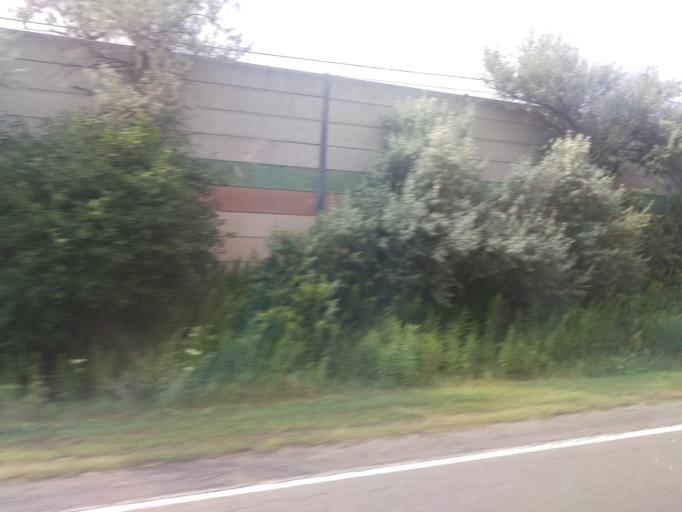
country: CA
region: Ontario
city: Mississauga
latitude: 43.5291
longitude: -79.6419
